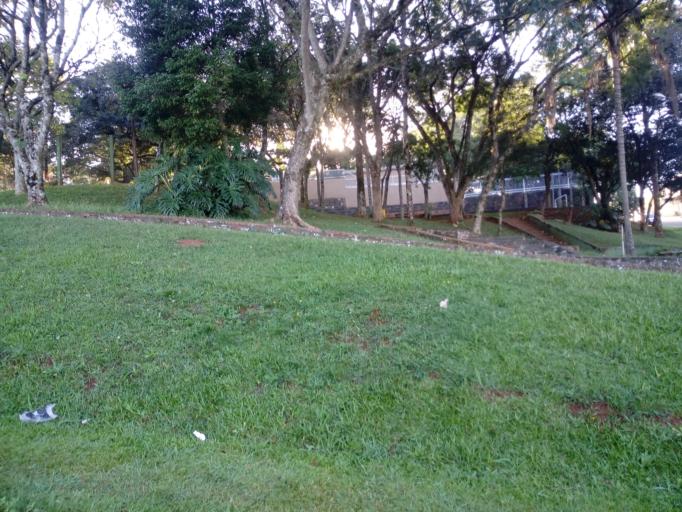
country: BR
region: Santa Catarina
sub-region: Chapeco
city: Chapeco
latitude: -27.1155
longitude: -52.6134
